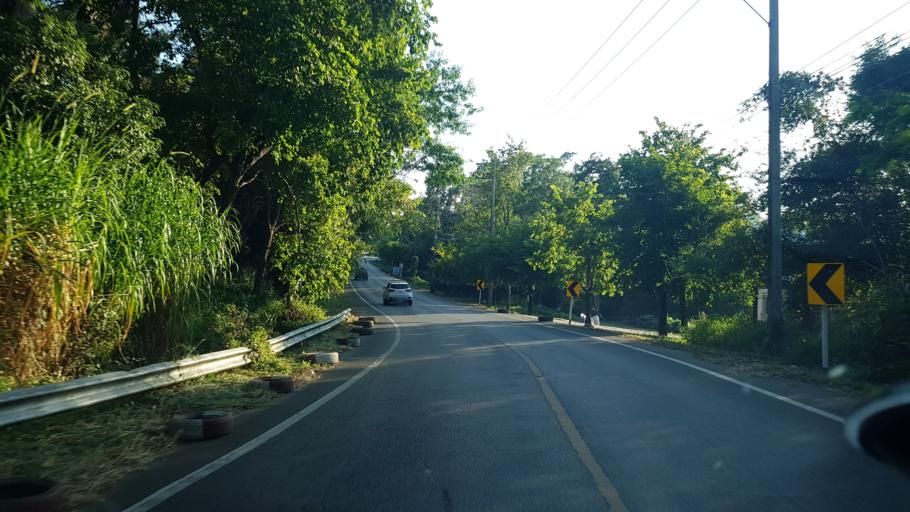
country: TH
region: Chiang Rai
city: Mae Fa Luang
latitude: 20.3017
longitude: 99.8164
